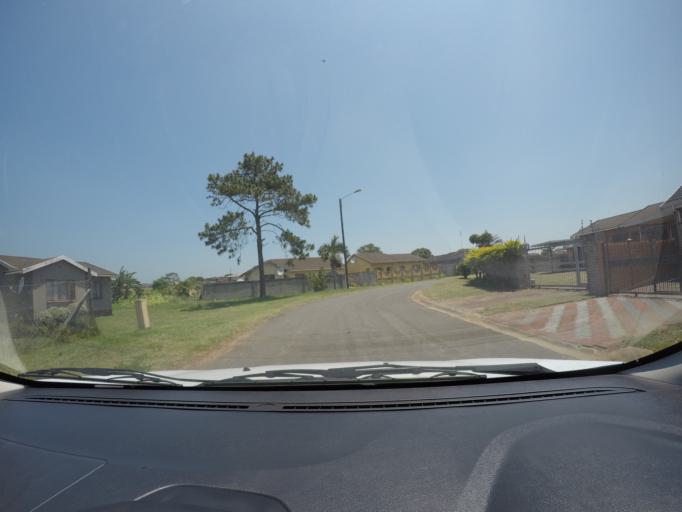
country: ZA
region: KwaZulu-Natal
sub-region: uThungulu District Municipality
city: eSikhawini
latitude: -28.8904
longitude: 31.8844
